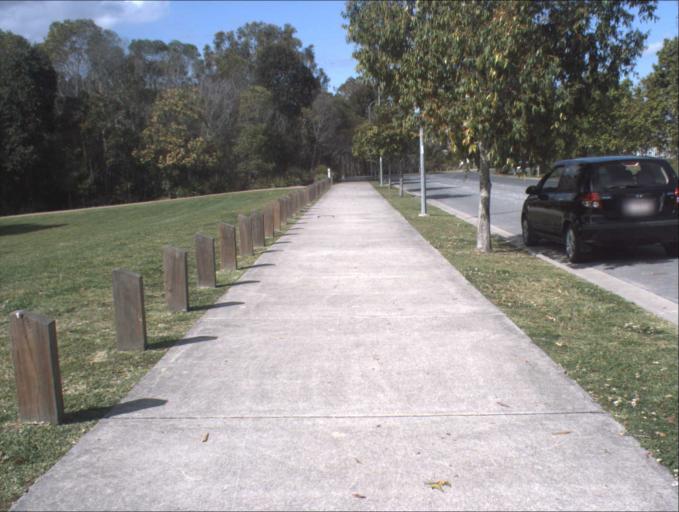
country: AU
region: Queensland
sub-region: Logan
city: Woodridge
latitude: -27.6684
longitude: 153.0794
